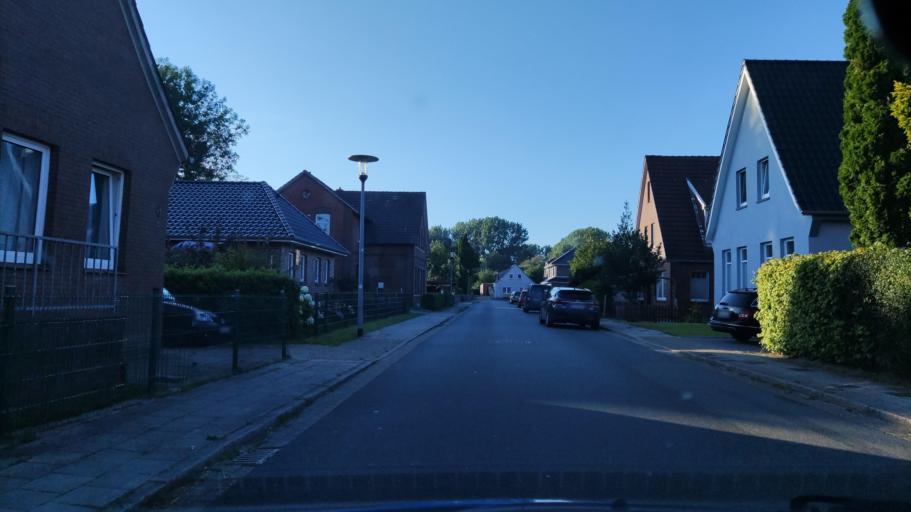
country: DE
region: Lower Saxony
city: Wittmund
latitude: 53.5773
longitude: 7.7894
